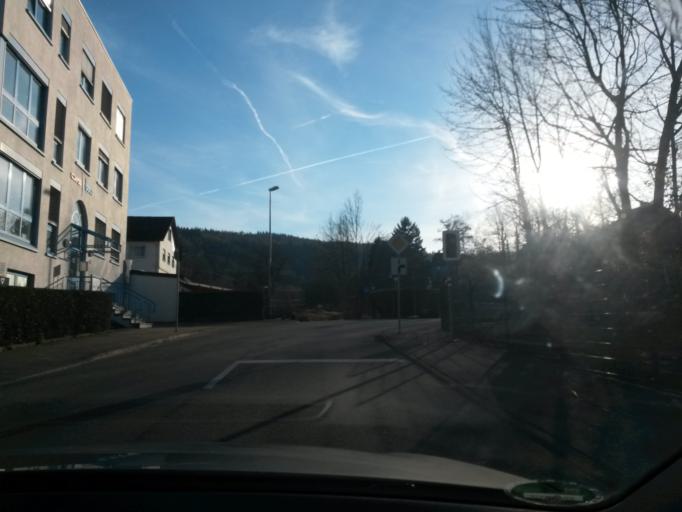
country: DE
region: Baden-Wuerttemberg
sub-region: Karlsruhe Region
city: Birkenfeld
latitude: 48.8710
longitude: 8.6461
